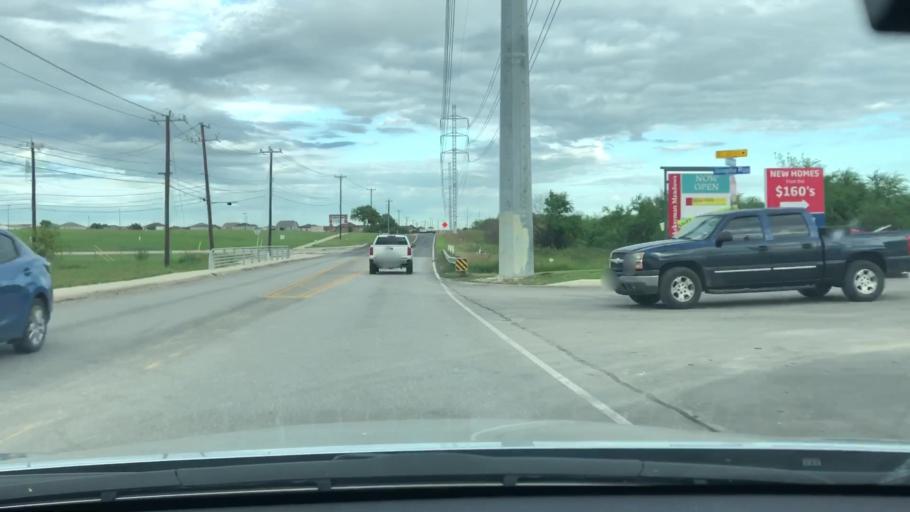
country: US
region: Texas
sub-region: Bexar County
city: Kirby
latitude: 29.4675
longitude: -98.3439
